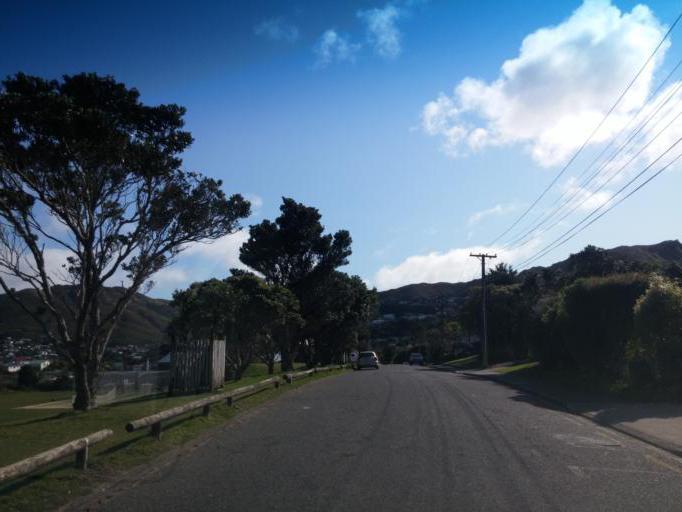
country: NZ
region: Wellington
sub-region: Wellington City
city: Wellington
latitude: -41.2491
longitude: 174.7859
